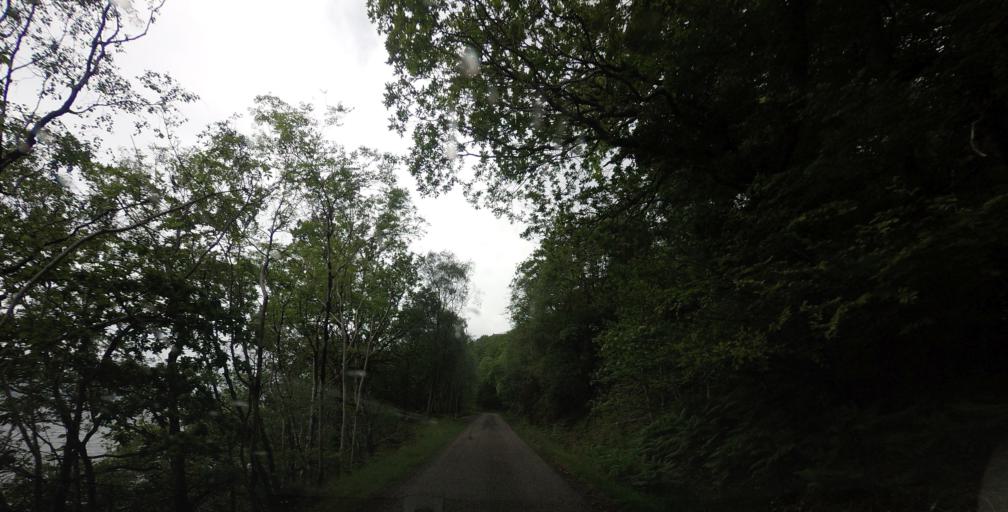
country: GB
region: Scotland
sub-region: Highland
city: Fort William
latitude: 56.7846
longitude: -5.1880
